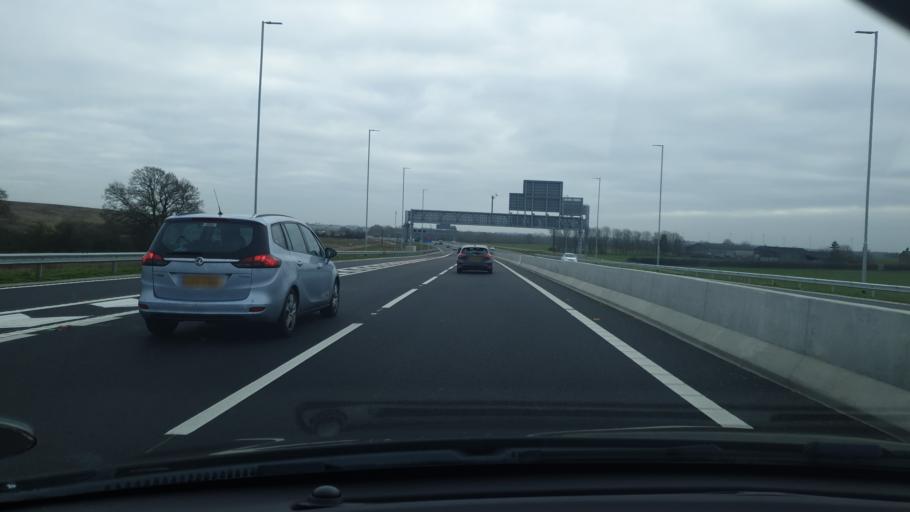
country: GB
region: England
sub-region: Cambridgeshire
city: Buckden
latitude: 52.3046
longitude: -0.2350
